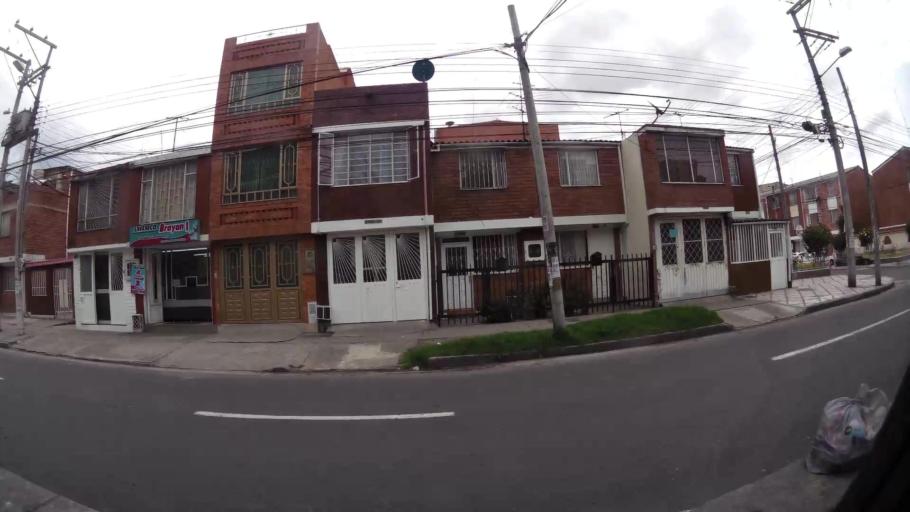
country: CO
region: Cundinamarca
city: Funza
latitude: 4.7066
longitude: -74.1231
